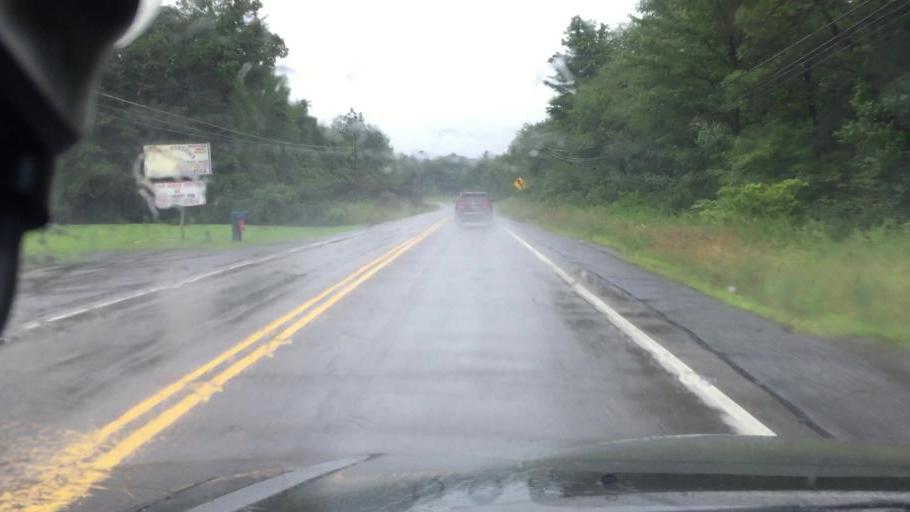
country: US
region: Pennsylvania
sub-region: Luzerne County
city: Freeland
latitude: 41.0179
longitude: -75.8843
